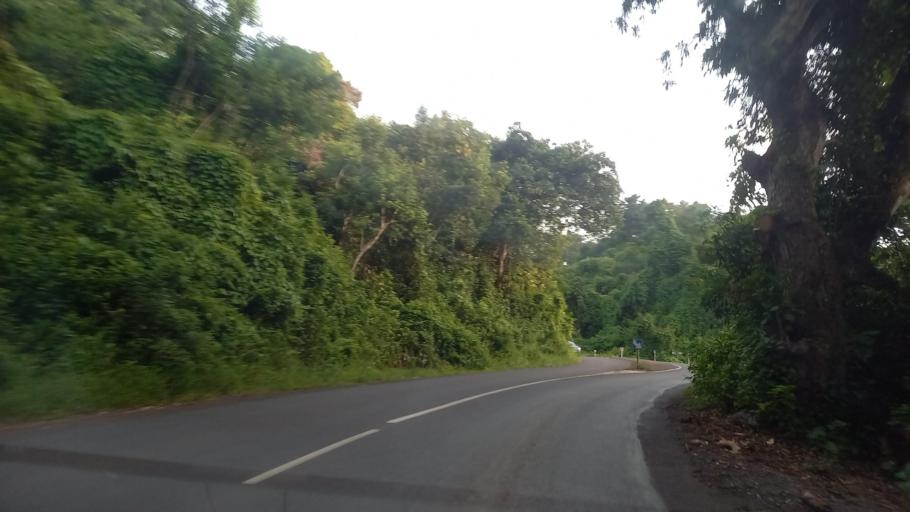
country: YT
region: Bandraboua
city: Bandraboua
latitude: -12.7349
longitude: 45.1189
